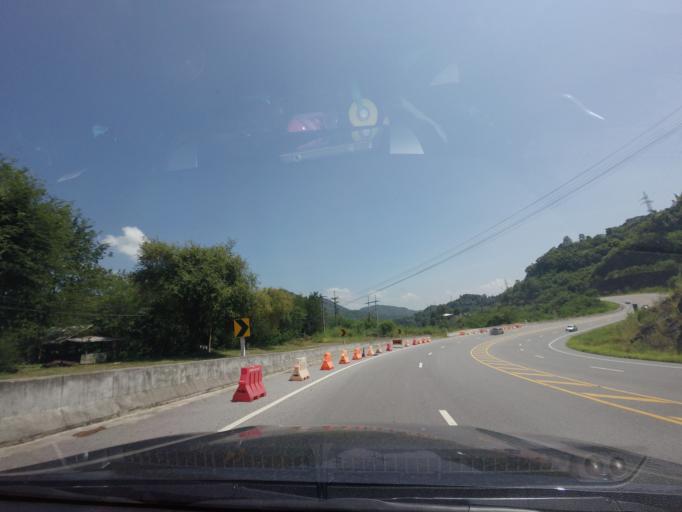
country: TH
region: Phetchabun
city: Lom Sak
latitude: 16.7814
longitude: 101.1039
